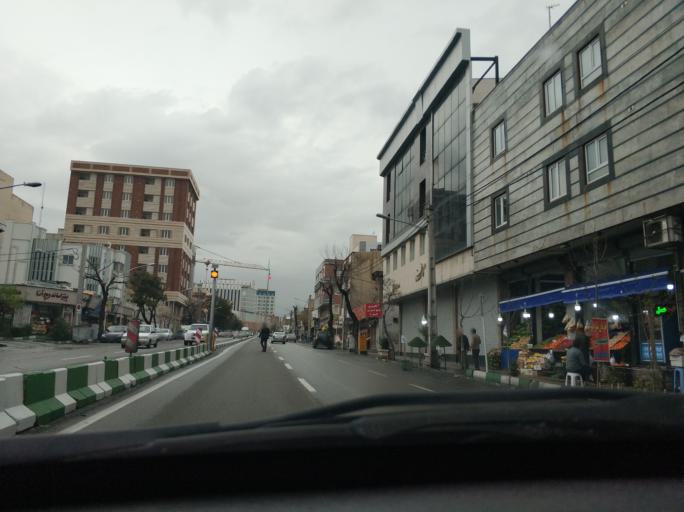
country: IR
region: Tehran
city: Tehran
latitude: 35.7035
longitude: 51.4392
